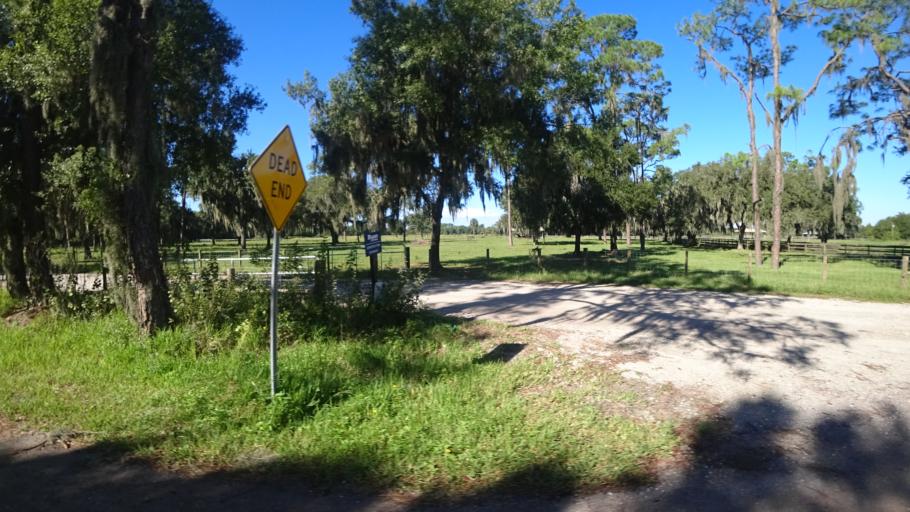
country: US
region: Florida
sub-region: Manatee County
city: Ellenton
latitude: 27.5758
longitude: -82.4418
